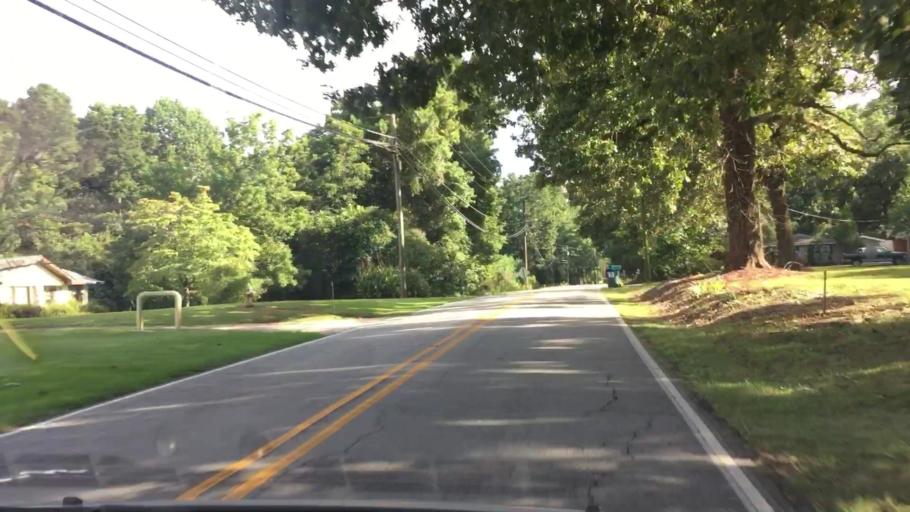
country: US
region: Georgia
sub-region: Henry County
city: Stockbridge
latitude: 33.6050
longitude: -84.1880
